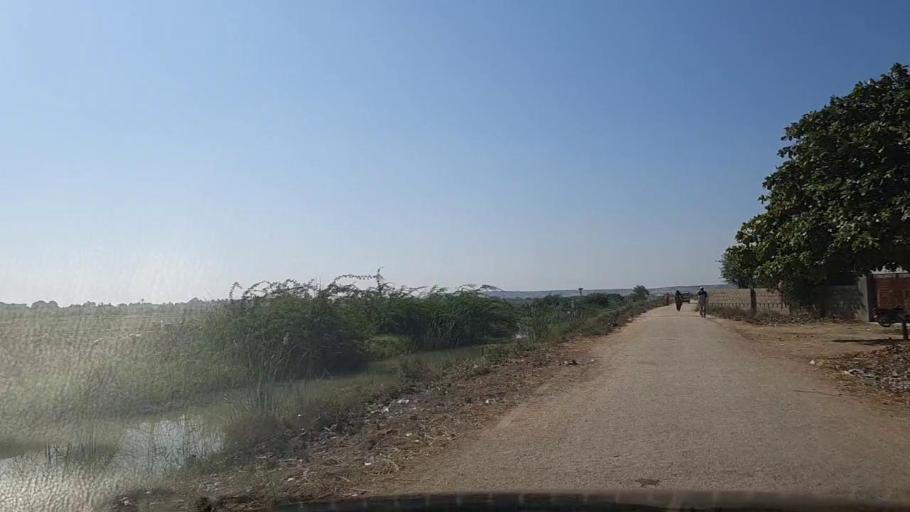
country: PK
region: Sindh
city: Thatta
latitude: 24.6337
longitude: 67.8731
